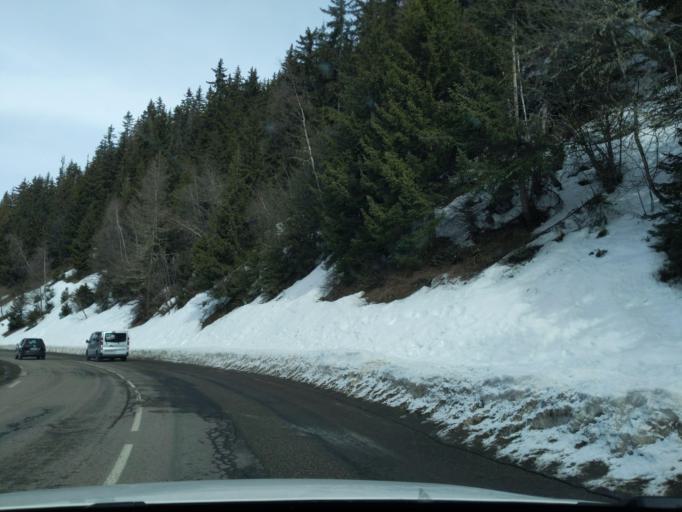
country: FR
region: Rhone-Alpes
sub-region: Departement de la Savoie
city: Bourg-Saint-Maurice
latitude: 45.5796
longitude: 6.7880
